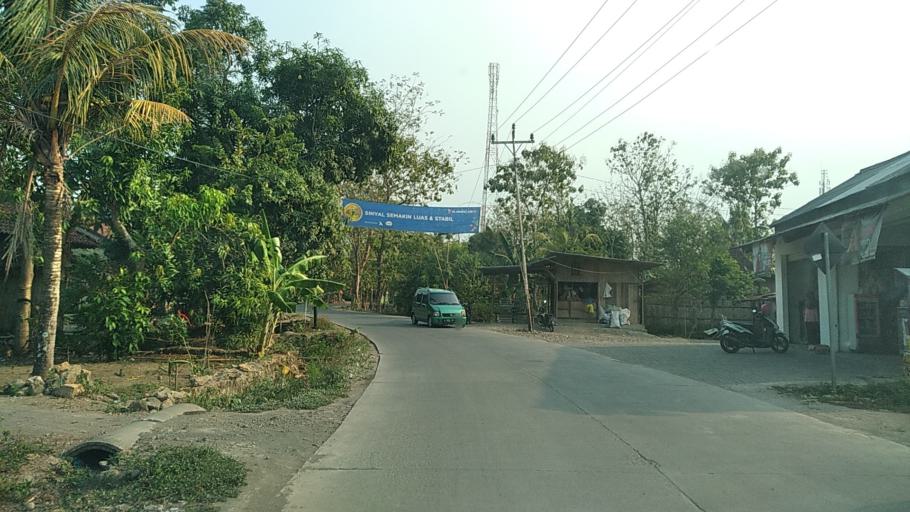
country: ID
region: Central Java
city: Mranggen
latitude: -7.0645
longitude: 110.4992
